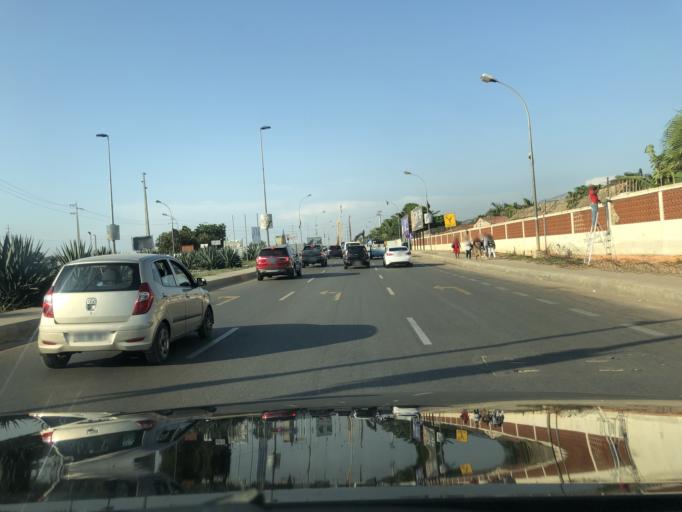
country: AO
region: Luanda
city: Luanda
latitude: -8.9106
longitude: 13.1783
